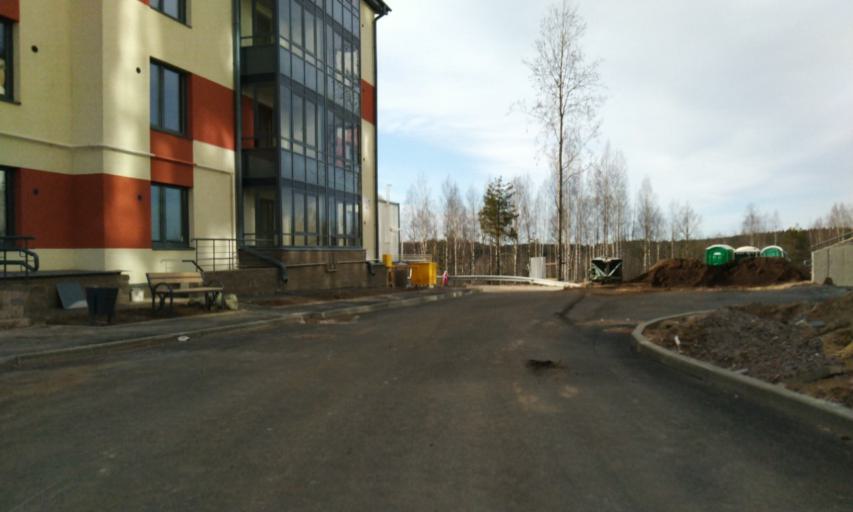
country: RU
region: Leningrad
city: Bugry
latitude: 60.1220
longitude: 30.4211
